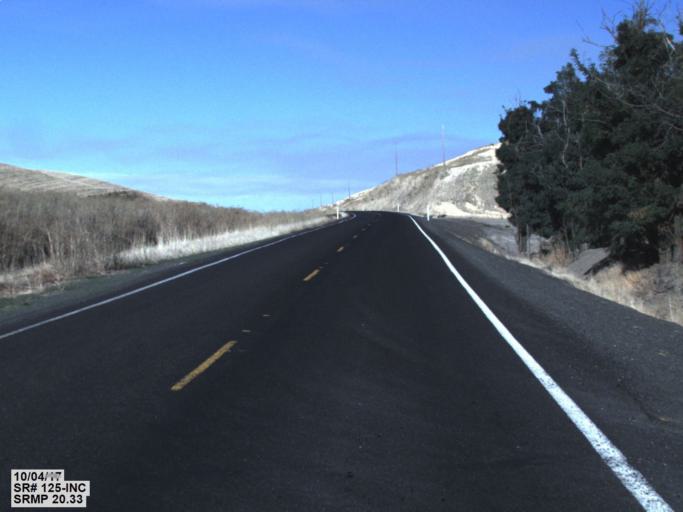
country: US
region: Washington
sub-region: Walla Walla County
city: Walla Walla
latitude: 46.2531
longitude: -118.3588
